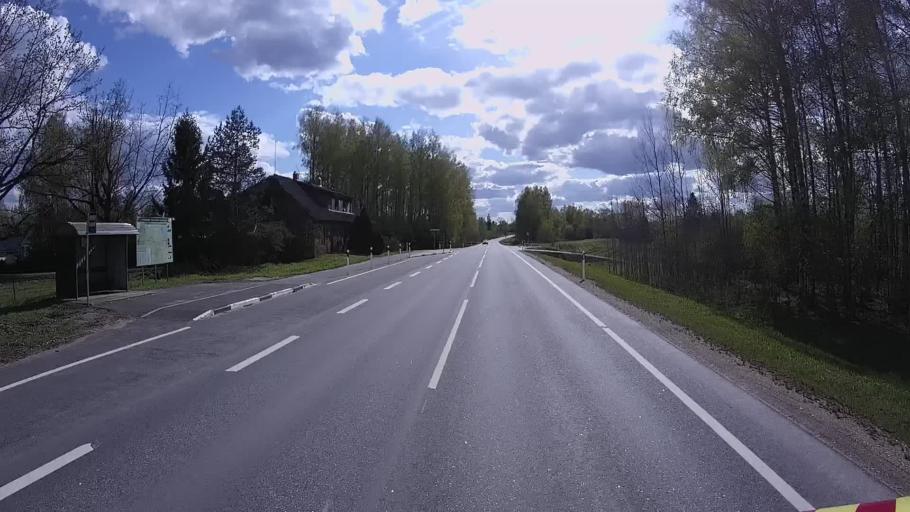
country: EE
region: Jogevamaa
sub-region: Mustvee linn
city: Mustvee
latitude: 58.8366
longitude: 26.8089
